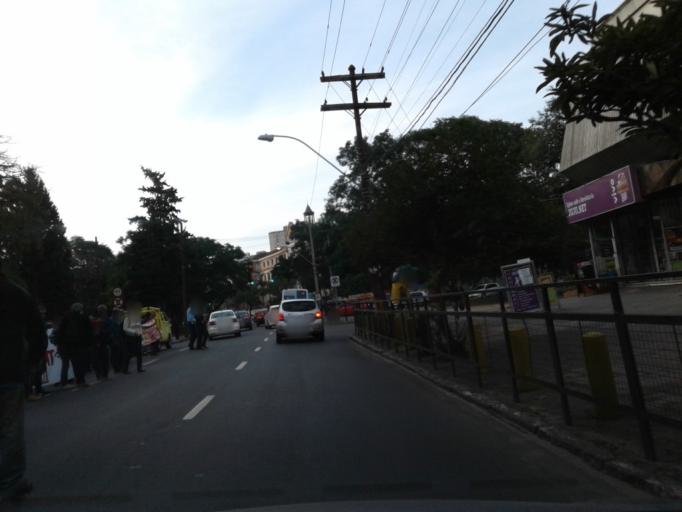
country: BR
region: Rio Grande do Sul
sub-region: Porto Alegre
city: Porto Alegre
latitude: -30.0421
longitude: -51.2279
